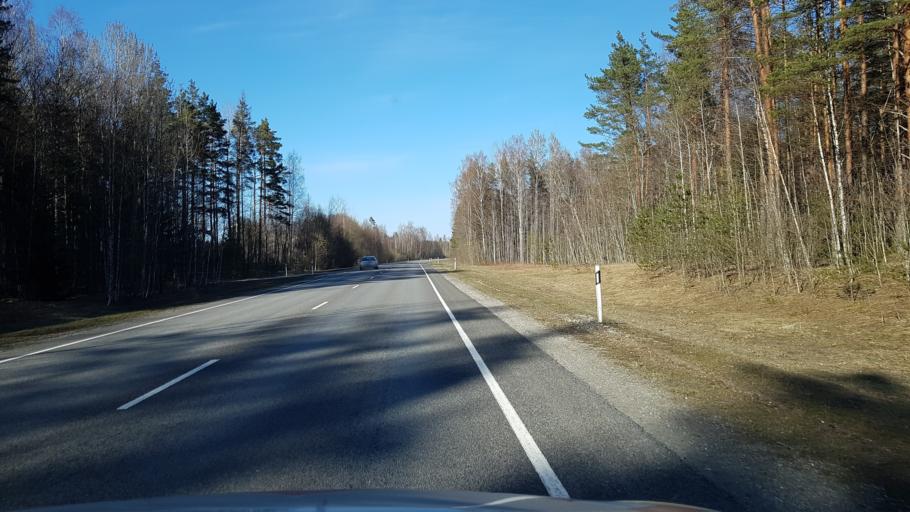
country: EE
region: Ida-Virumaa
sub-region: Kohtla-Nomme vald
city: Kohtla-Nomme
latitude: 59.0378
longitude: 27.2460
